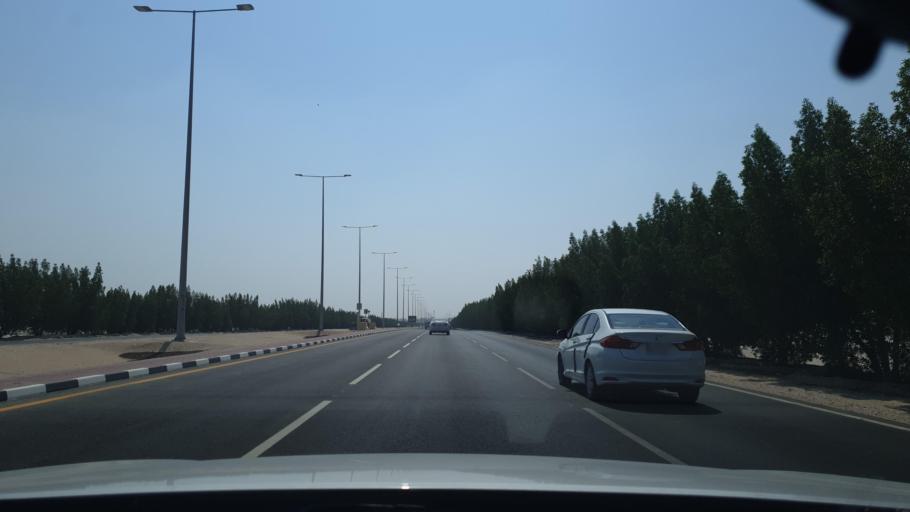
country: QA
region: Al Khawr
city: Al Khawr
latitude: 25.7043
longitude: 51.5041
